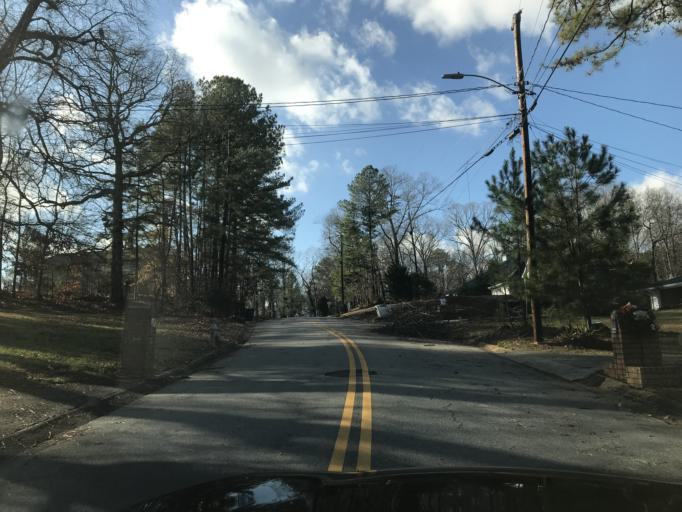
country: US
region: Georgia
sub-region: Fulton County
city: College Park
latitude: 33.6442
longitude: -84.4769
